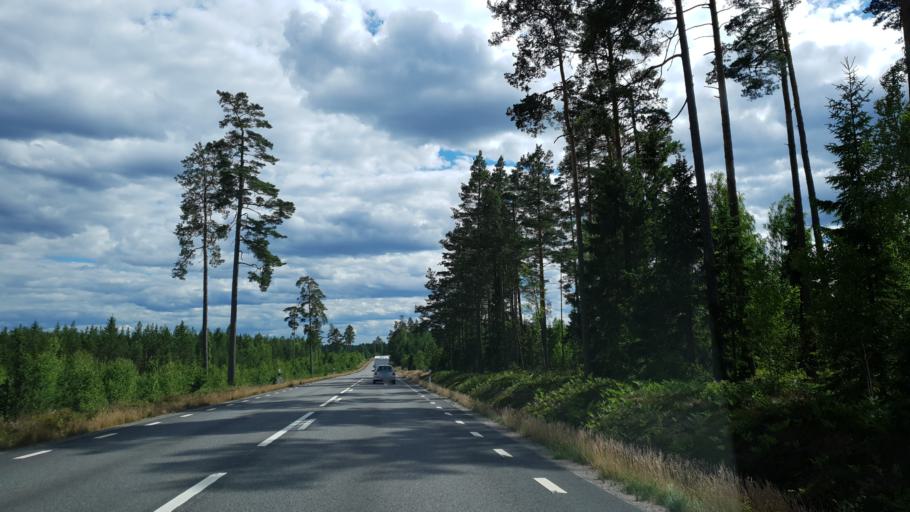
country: SE
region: Kronoberg
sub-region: Lessebo Kommun
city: Lessebo
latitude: 56.8106
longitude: 15.4117
